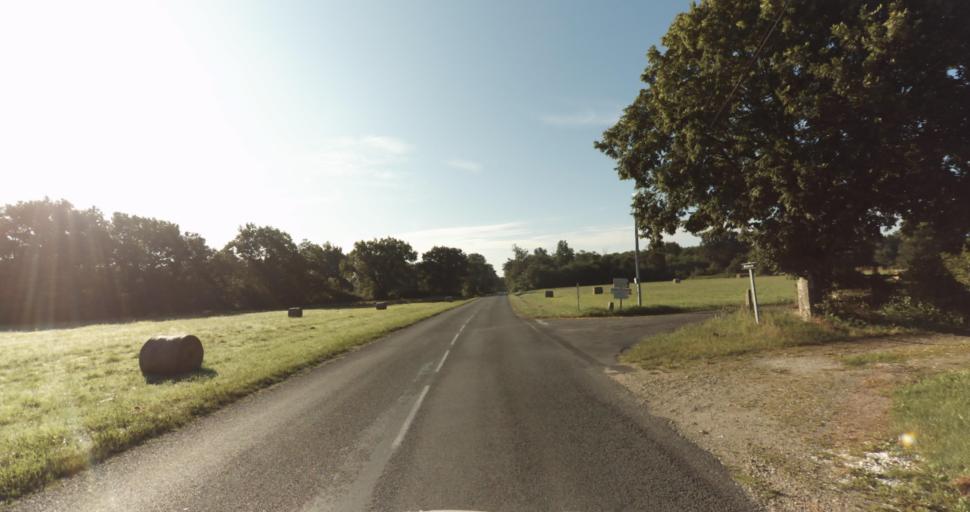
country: FR
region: Aquitaine
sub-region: Departement de la Gironde
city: Bazas
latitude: 44.4118
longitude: -0.2129
